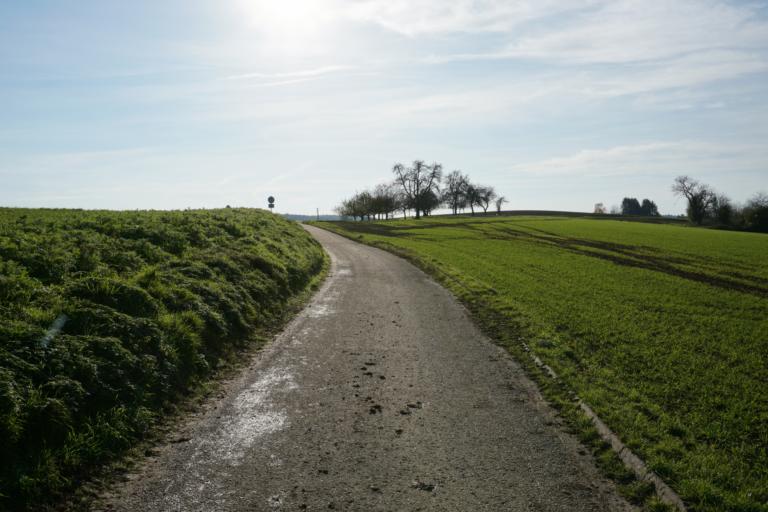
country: DE
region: Baden-Wuerttemberg
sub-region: Karlsruhe Region
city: Aglasterhausen
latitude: 49.3626
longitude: 9.0037
